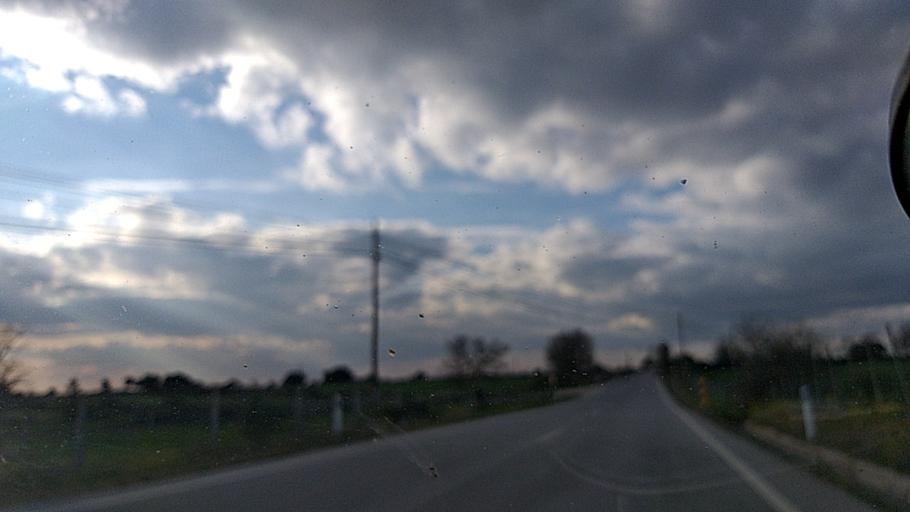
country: ES
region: Castille and Leon
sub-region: Provincia de Salamanca
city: Aldea del Obispo
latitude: 40.6963
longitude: -6.8848
